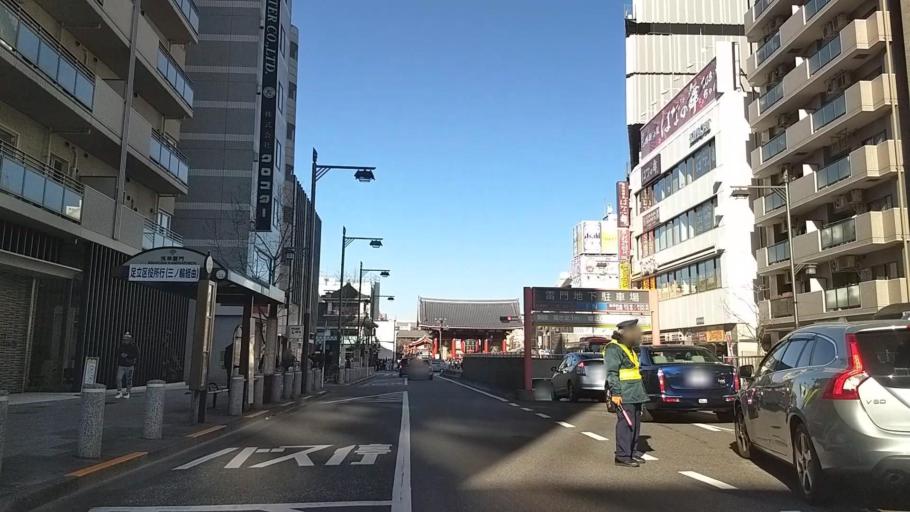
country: JP
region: Tokyo
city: Urayasu
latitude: 35.7102
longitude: 139.7962
